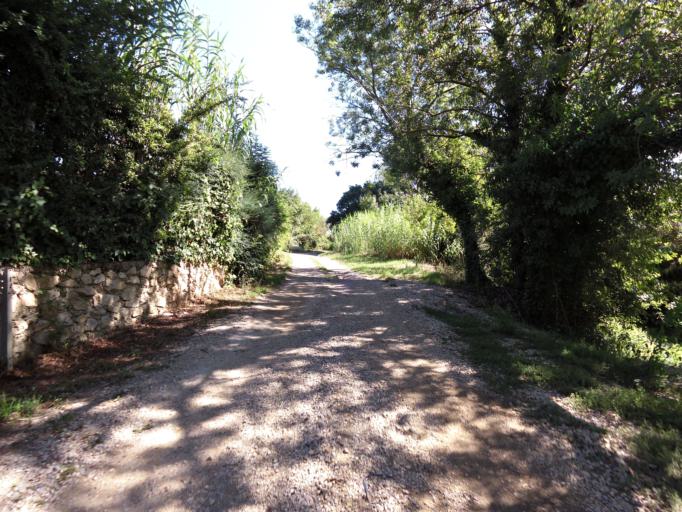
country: FR
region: Languedoc-Roussillon
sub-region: Departement du Gard
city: Vergeze
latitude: 43.7423
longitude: 4.2127
